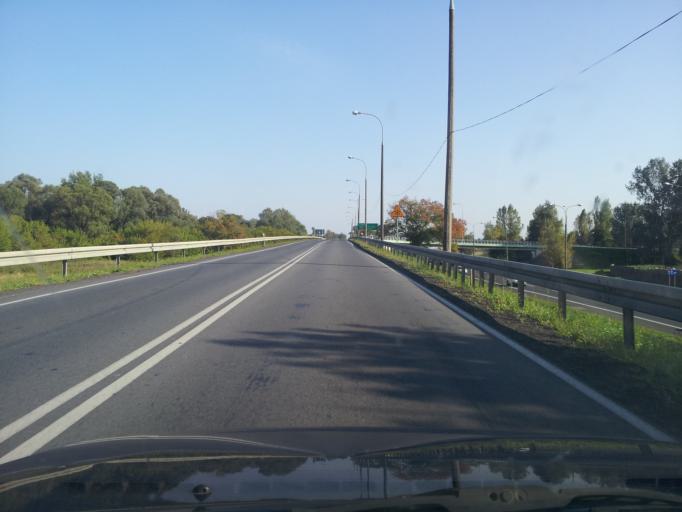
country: PL
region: Masovian Voivodeship
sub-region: Powiat nowodworski
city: Nowy Dwor Mazowiecki
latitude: 52.4123
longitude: 20.6962
